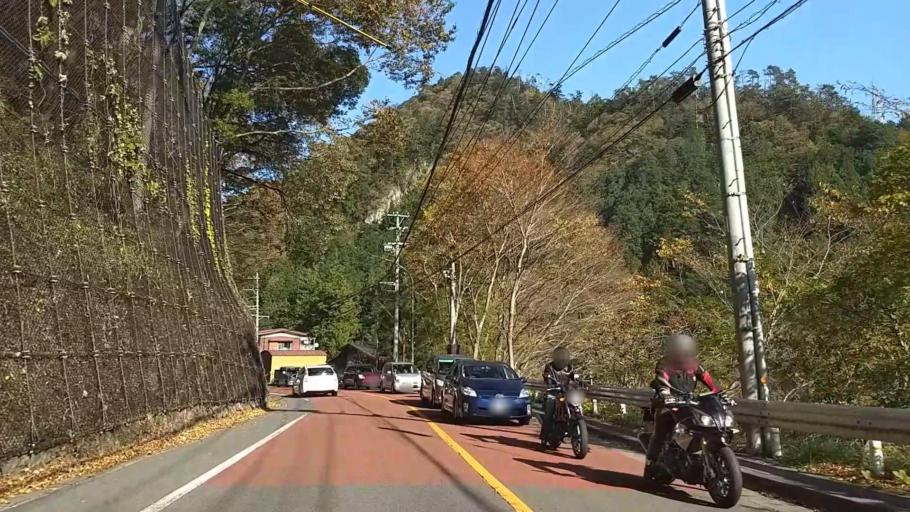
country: JP
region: Tokyo
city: Itsukaichi
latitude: 35.8038
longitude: 139.1090
